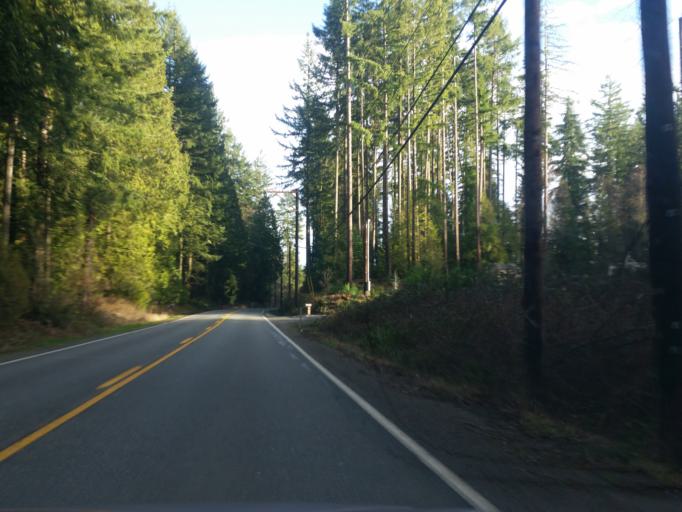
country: US
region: Washington
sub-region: Snohomish County
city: North Creek
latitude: 47.8099
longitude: -122.1684
